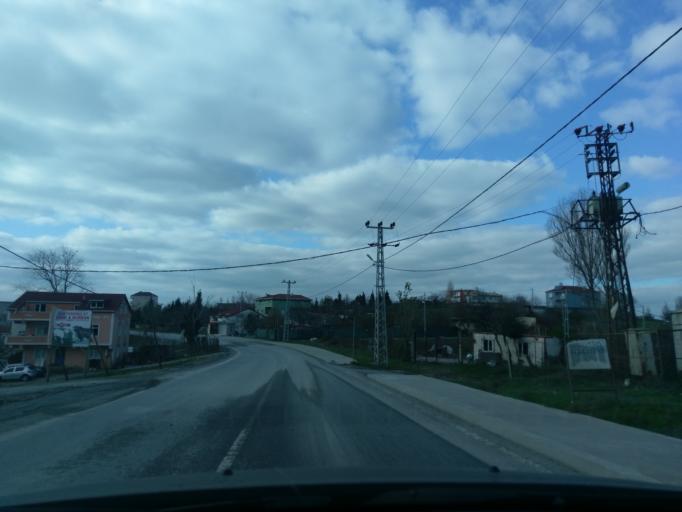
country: TR
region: Istanbul
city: Durusu
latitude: 41.2641
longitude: 28.6827
